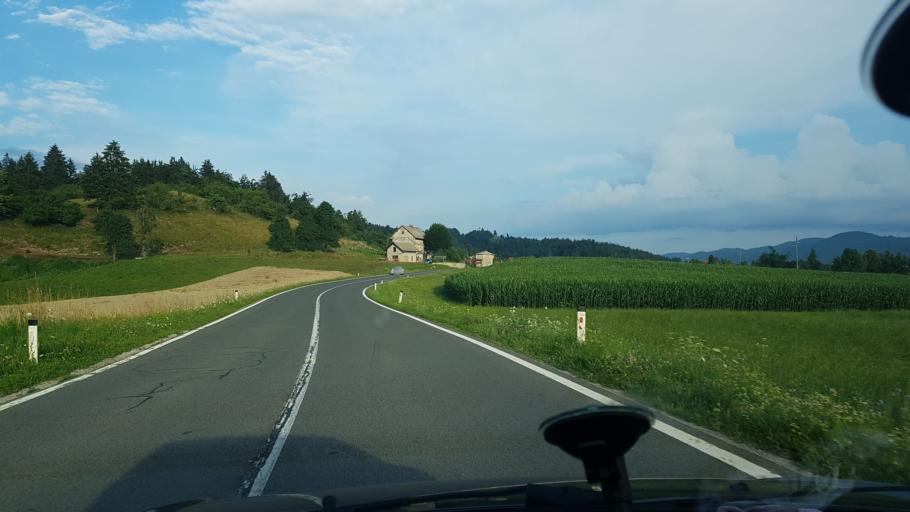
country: SI
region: Logatec
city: Logatec
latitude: 45.9335
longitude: 14.1324
